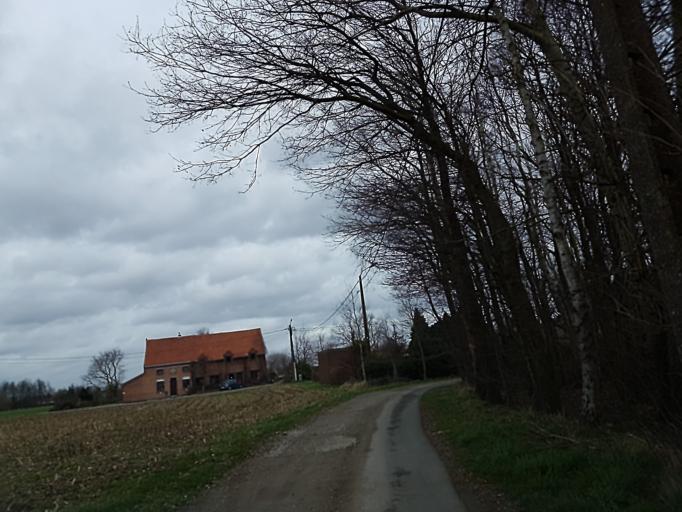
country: BE
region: Flanders
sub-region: Provincie Vlaams-Brabant
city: Zemst
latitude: 50.9886
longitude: 4.4331
